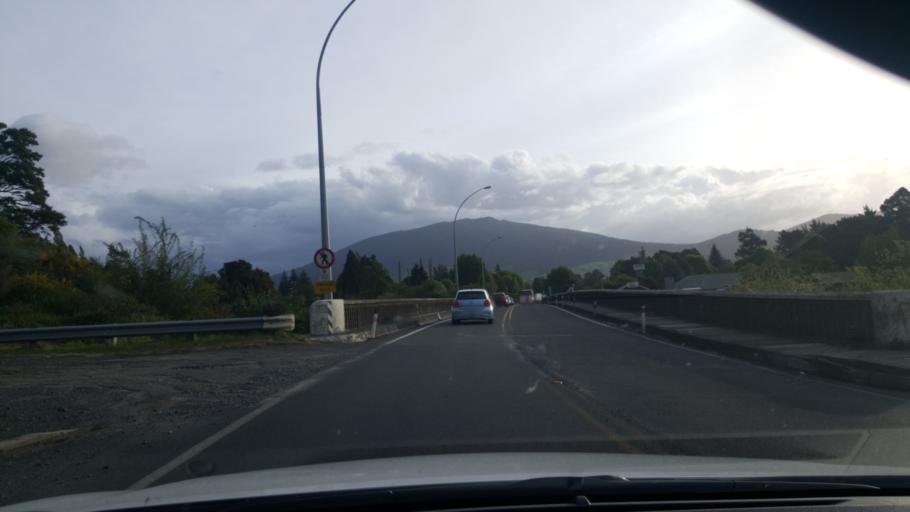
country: NZ
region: Waikato
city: Turangi
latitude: -38.9853
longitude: 175.8197
